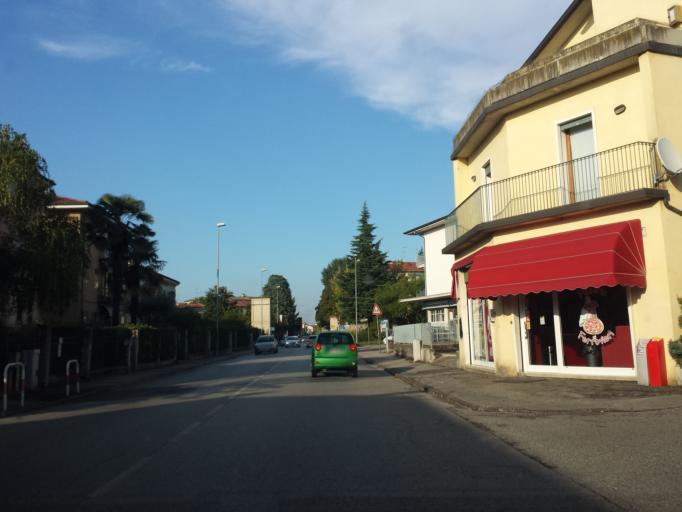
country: IT
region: Veneto
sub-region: Provincia di Vicenza
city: Vicenza
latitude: 45.5356
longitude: 11.5239
